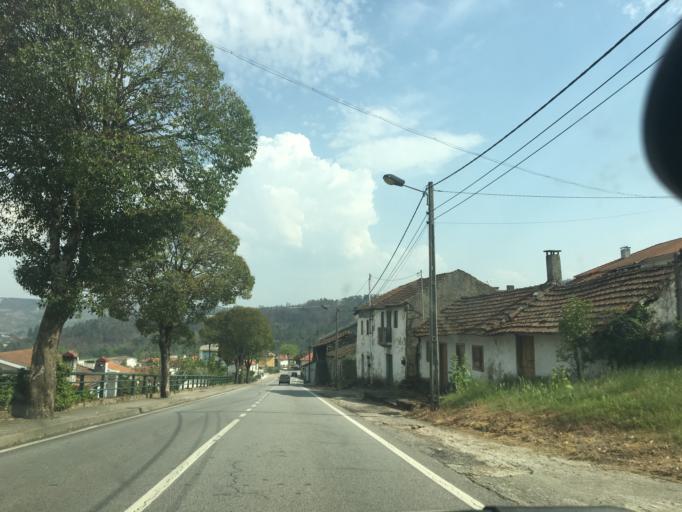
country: PT
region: Vila Real
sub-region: Boticas
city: Boticas
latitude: 41.6888
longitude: -7.6753
